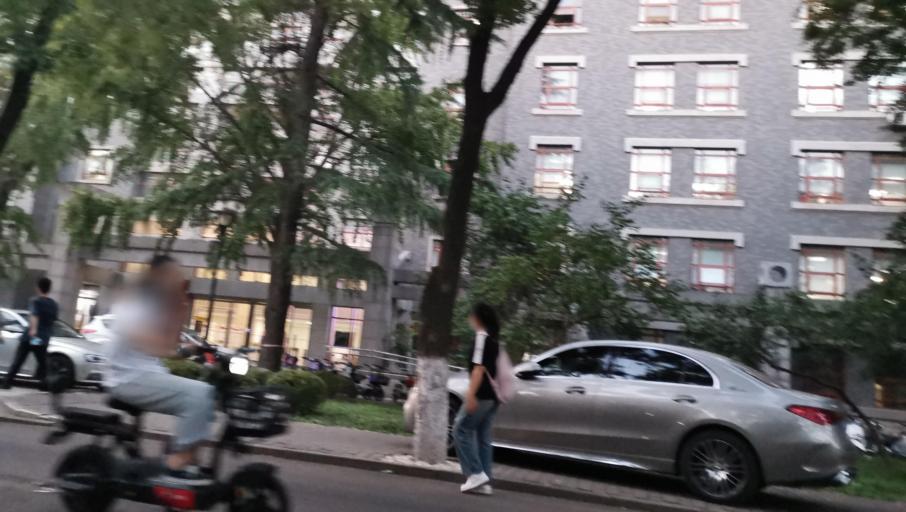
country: CN
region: Shandong Sheng
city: Jinan
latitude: 36.6538
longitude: 117.0139
